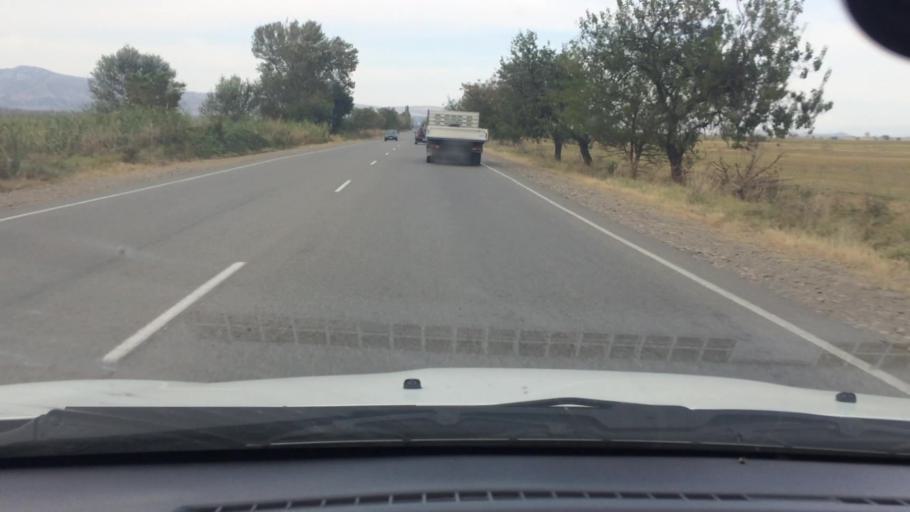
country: GE
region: Kvemo Kartli
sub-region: Marneuli
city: Marneuli
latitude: 41.5457
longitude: 44.7766
